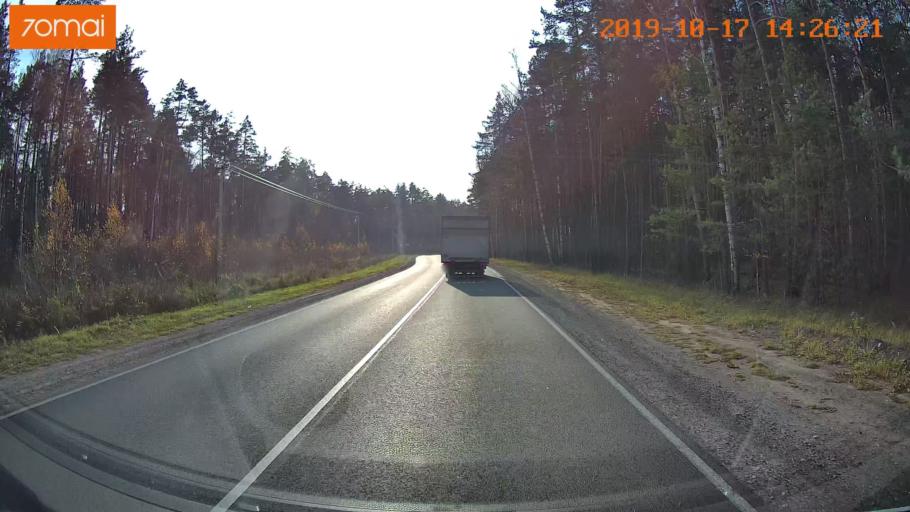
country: RU
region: Moskovskaya
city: Radovitskiy
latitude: 54.9927
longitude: 39.9682
